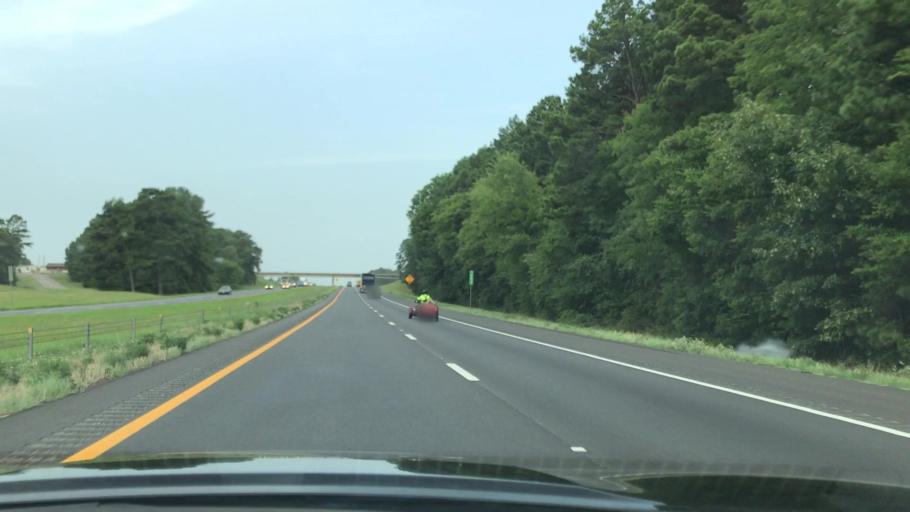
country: US
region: Texas
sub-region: Harrison County
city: Hallsville
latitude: 32.4676
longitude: -94.6165
